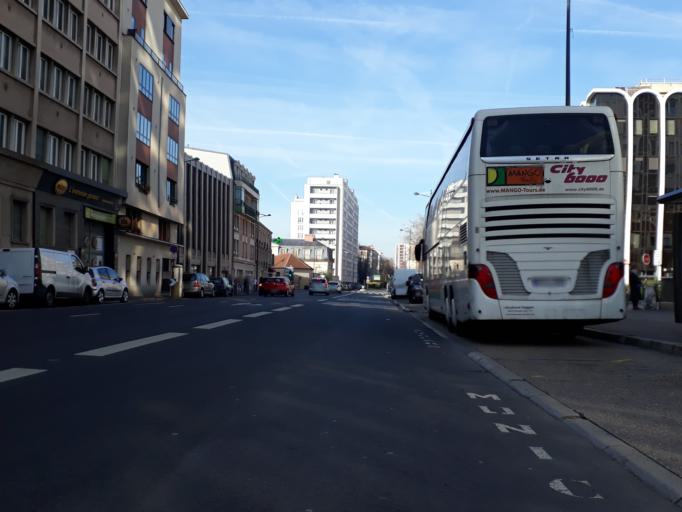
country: FR
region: Ile-de-France
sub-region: Departement des Hauts-de-Seine
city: Clichy
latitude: 48.9038
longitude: 2.3055
